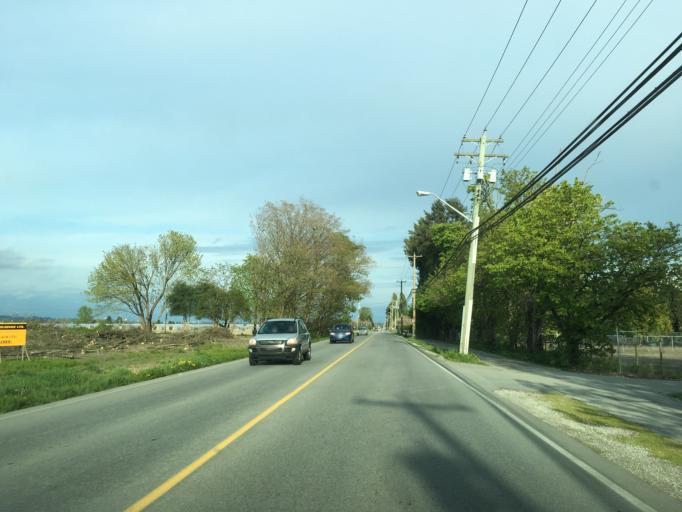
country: CA
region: British Columbia
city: Richmond
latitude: 49.1699
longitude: -123.0597
